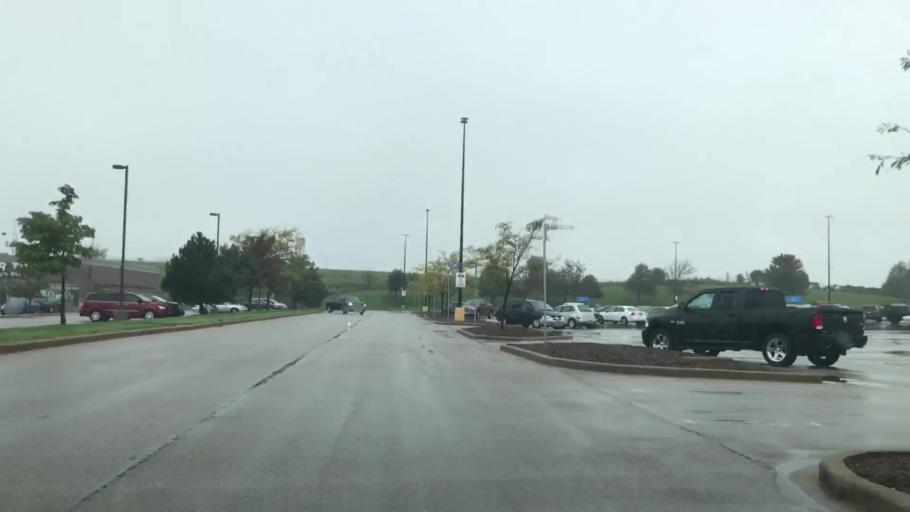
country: US
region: Wisconsin
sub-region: Dodge County
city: Beaver Dam
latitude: 43.4876
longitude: -88.8105
